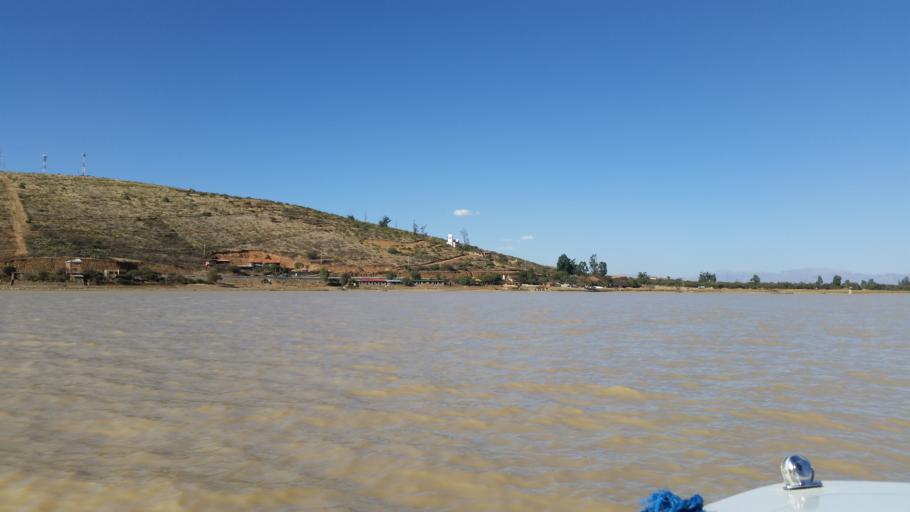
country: BO
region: Cochabamba
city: Tarata
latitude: -17.5351
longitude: -66.0876
